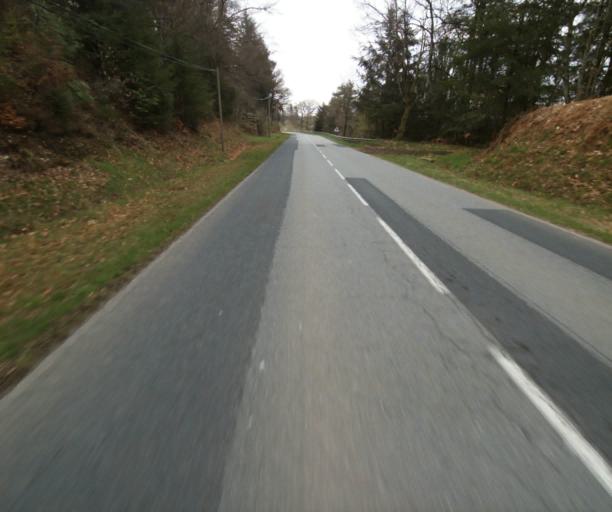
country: FR
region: Limousin
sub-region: Departement de la Correze
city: Correze
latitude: 45.3885
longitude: 1.8646
